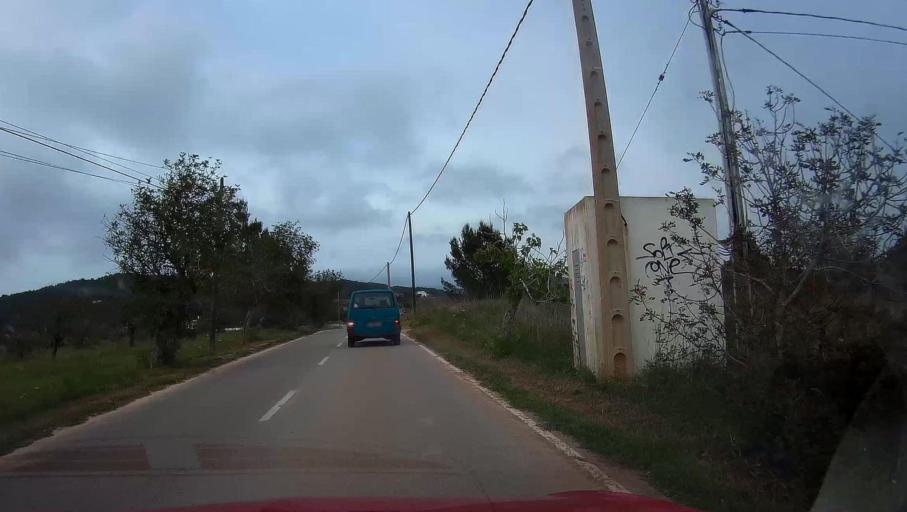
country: ES
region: Balearic Islands
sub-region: Illes Balears
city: Sant Joan de Labritja
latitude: 39.0472
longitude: 1.4181
